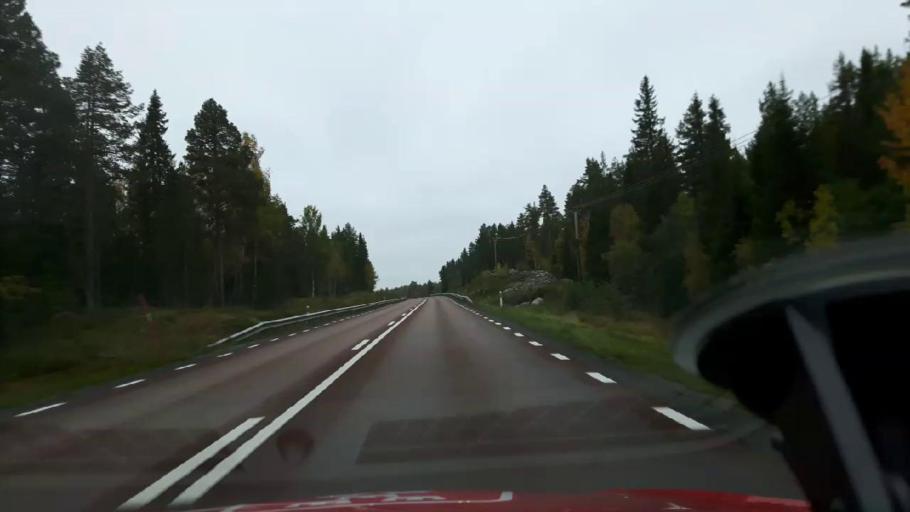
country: SE
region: Jaemtland
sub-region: Bergs Kommun
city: Hoverberg
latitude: 62.8668
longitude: 14.5201
